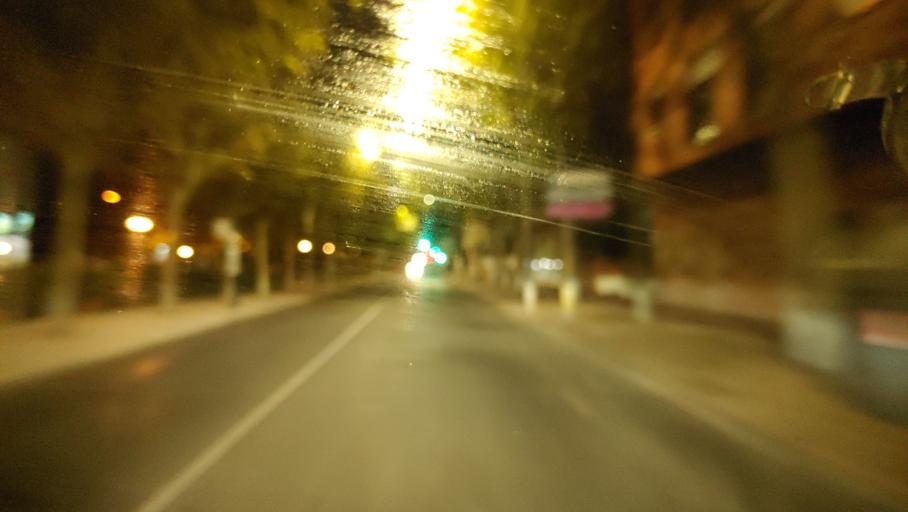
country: ES
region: Castille-La Mancha
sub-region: Provincia de Ciudad Real
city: Ciudad Real
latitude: 38.9743
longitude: -3.9268
